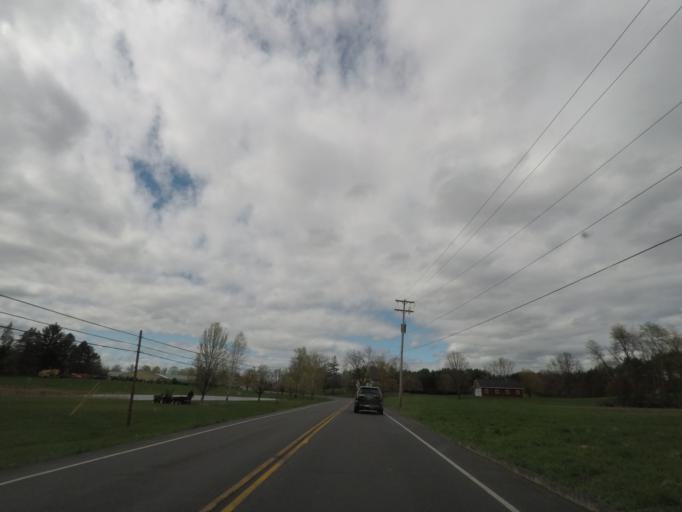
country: US
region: New York
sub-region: Columbia County
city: Chatham
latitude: 42.3711
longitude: -73.6217
